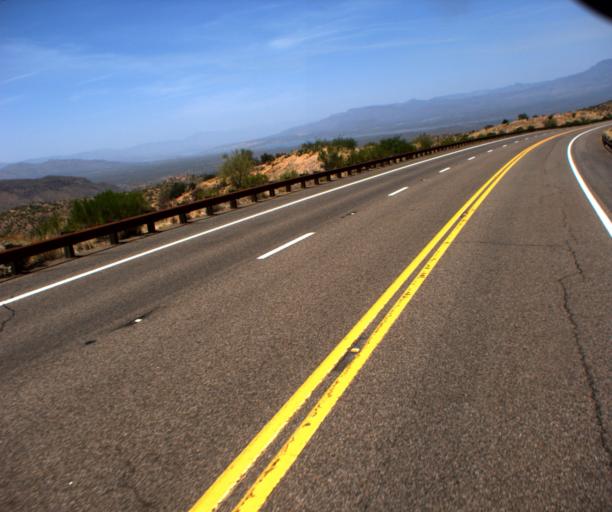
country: US
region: Arizona
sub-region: Gila County
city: Miami
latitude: 33.5517
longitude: -110.9480
